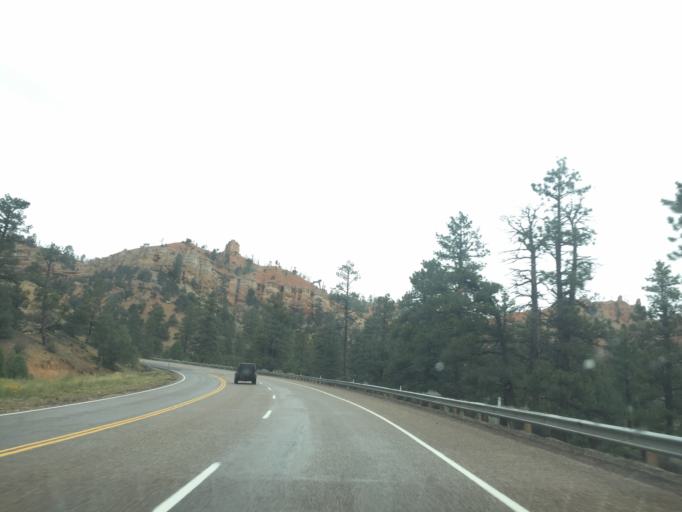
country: US
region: Utah
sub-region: Garfield County
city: Panguitch
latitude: 37.6840
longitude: -112.1141
